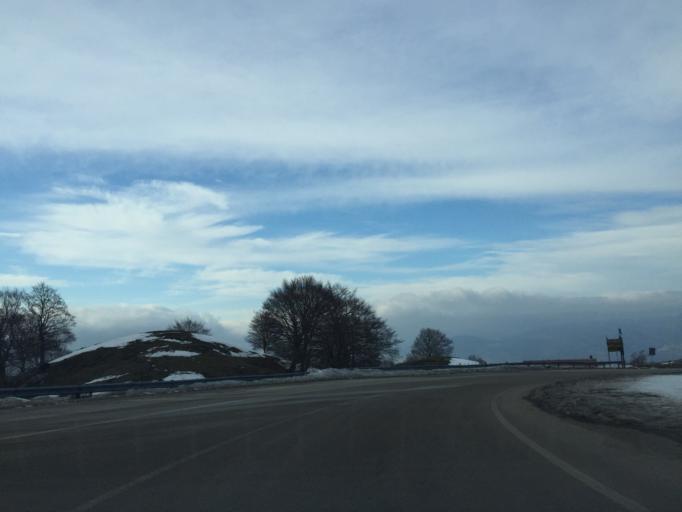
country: IT
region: Molise
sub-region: Provincia di Campobasso
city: San Massimo
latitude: 41.4660
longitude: 14.4148
